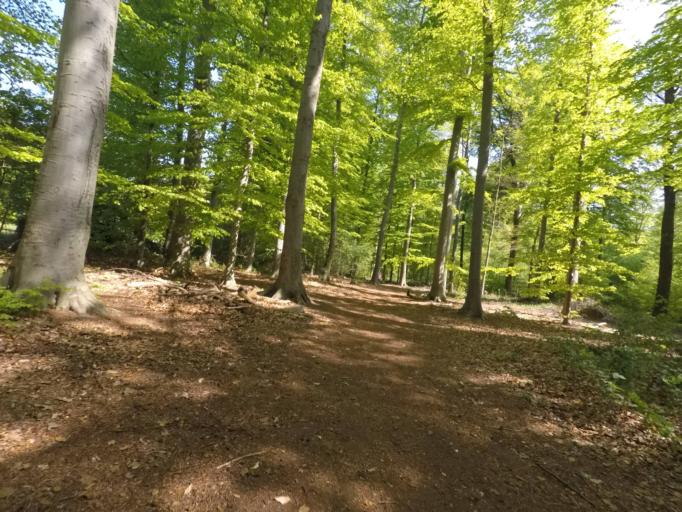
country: DE
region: North Rhine-Westphalia
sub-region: Regierungsbezirk Detmold
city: Bielefeld
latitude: 52.0101
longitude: 8.5773
